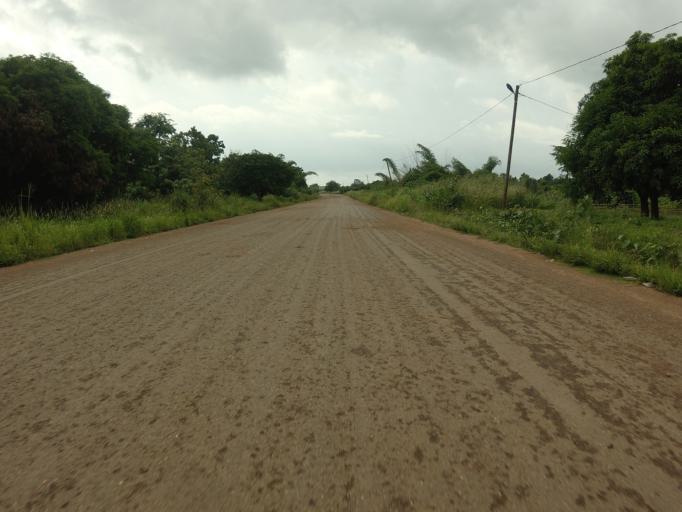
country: GH
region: Volta
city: Kpandu
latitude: 6.9461
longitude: 0.4604
